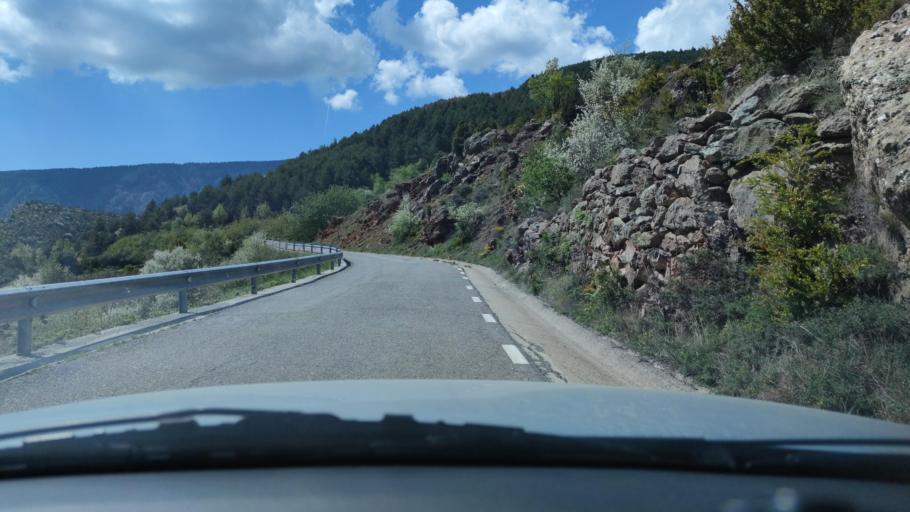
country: ES
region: Catalonia
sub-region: Provincia de Lleida
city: Coll de Nargo
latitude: 42.3109
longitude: 1.2816
